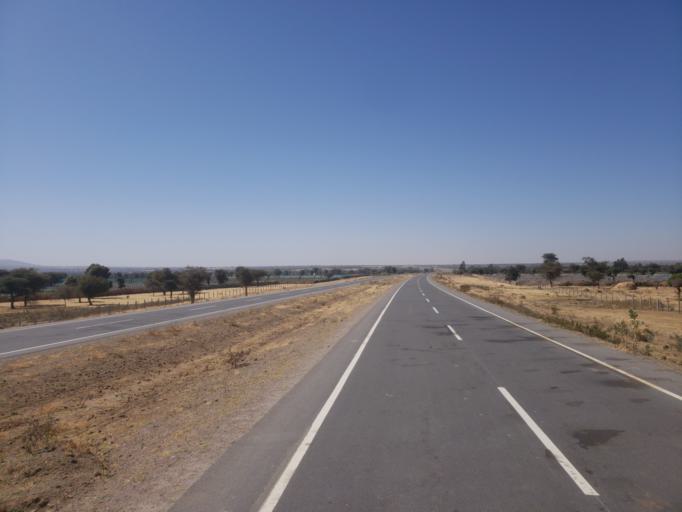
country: ET
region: Oromiya
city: Mojo
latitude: 8.3505
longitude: 38.9824
